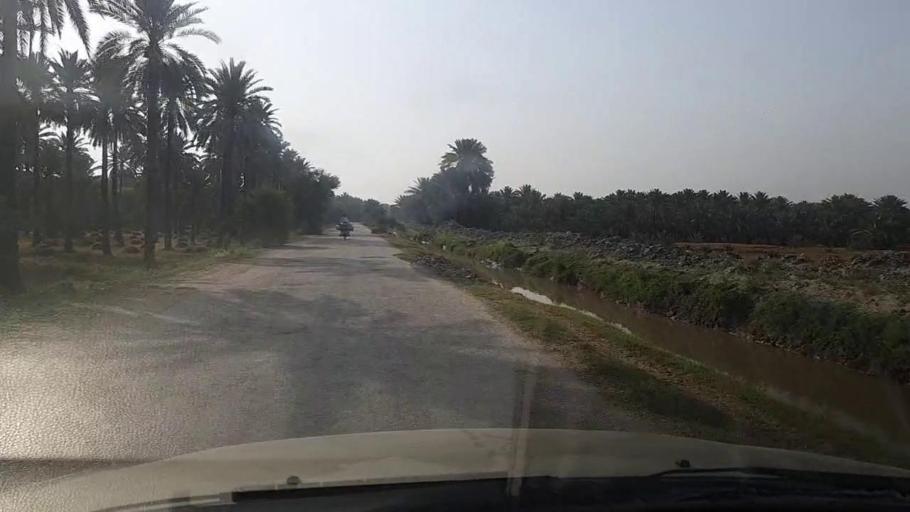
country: PK
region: Sindh
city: Pir jo Goth
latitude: 27.5606
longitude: 68.5438
